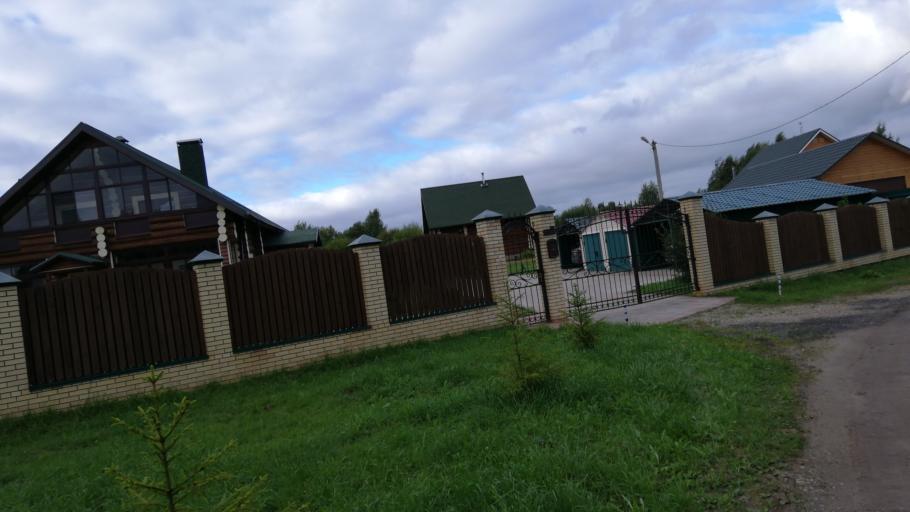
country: RU
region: Jaroslavl
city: Konstantinovskiy
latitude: 57.8023
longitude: 39.7160
